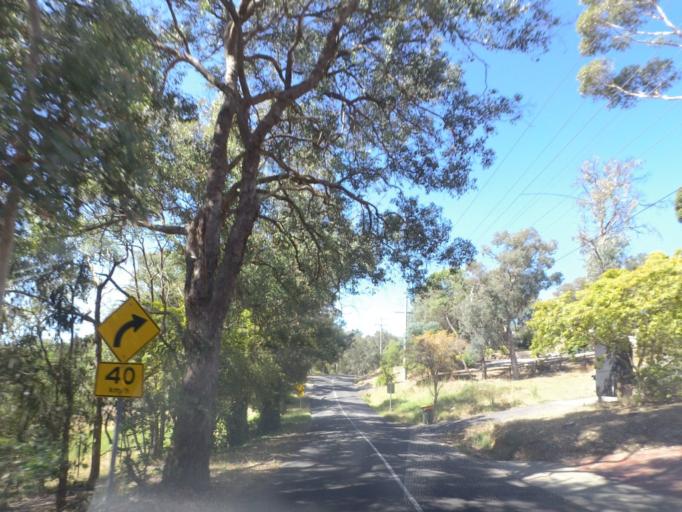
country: AU
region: Victoria
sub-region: Maroondah
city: Croydon Hills
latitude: -37.7501
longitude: 145.2670
